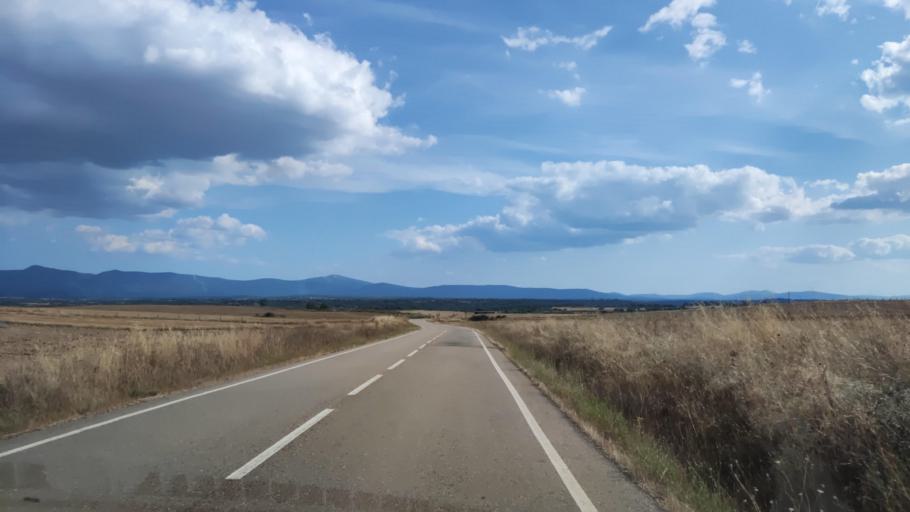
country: ES
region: Castille and Leon
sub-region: Provincia de Salamanca
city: Pastores
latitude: 40.5092
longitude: -6.5049
